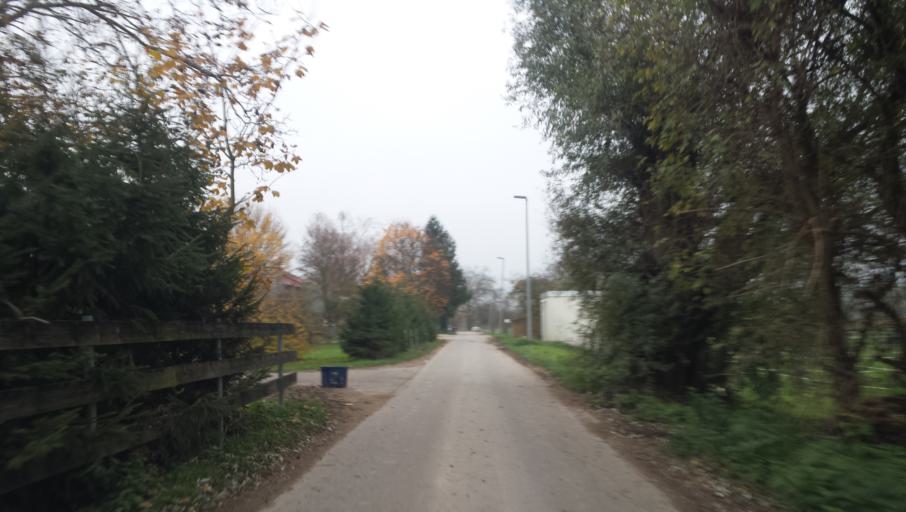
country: DE
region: Baden-Wuerttemberg
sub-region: Karlsruhe Region
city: Ketsch
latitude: 49.3482
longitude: 8.5057
